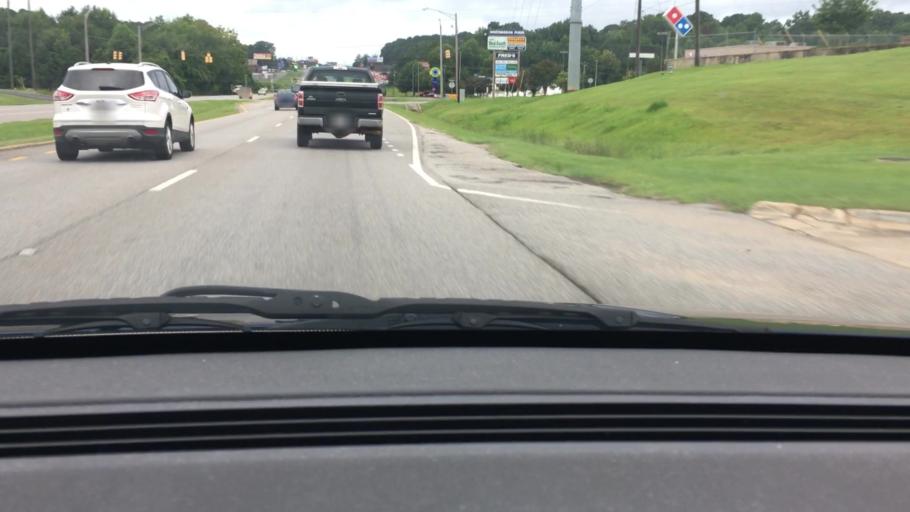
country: US
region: Alabama
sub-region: Tuscaloosa County
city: Northport
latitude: 33.2370
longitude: -87.5597
